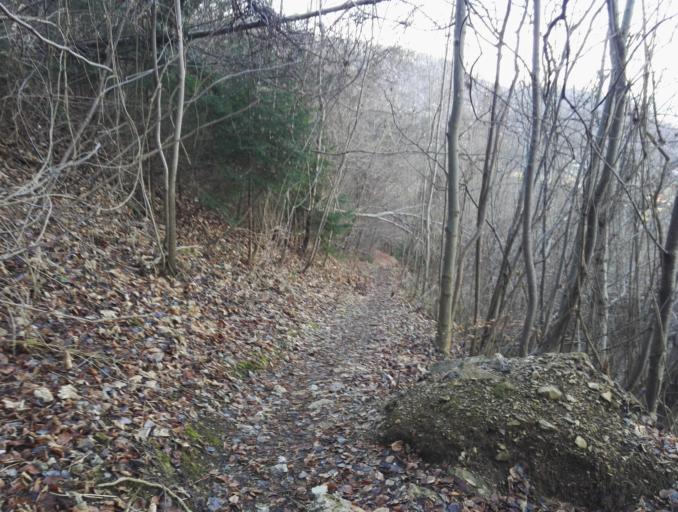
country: AT
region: Styria
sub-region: Graz Stadt
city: Goesting
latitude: 47.1051
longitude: 15.3787
